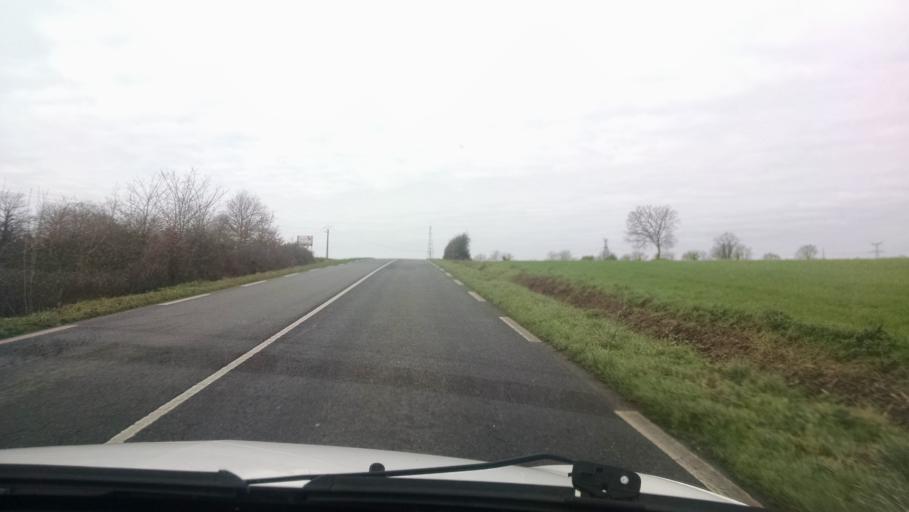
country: FR
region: Pays de la Loire
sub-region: Departement de la Loire-Atlantique
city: Getigne
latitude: 47.0728
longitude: -1.2236
